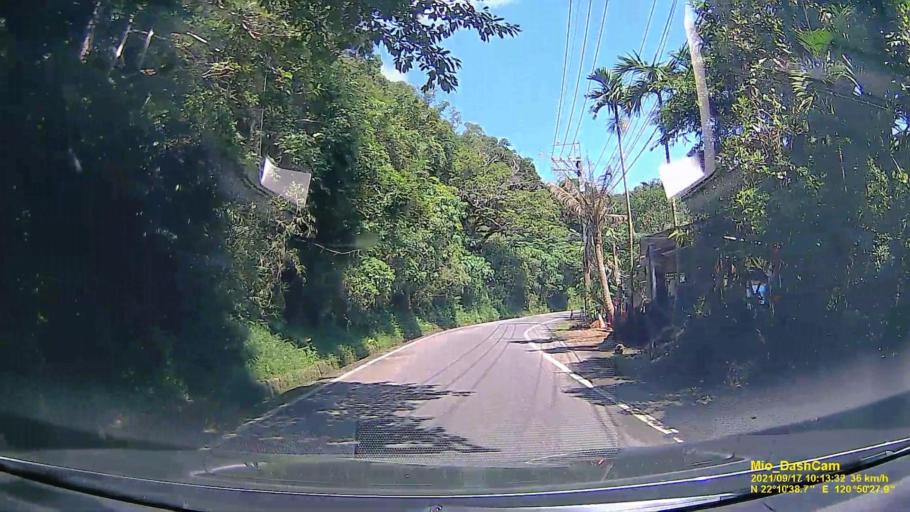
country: TW
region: Taiwan
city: Hengchun
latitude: 22.1774
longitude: 120.8411
